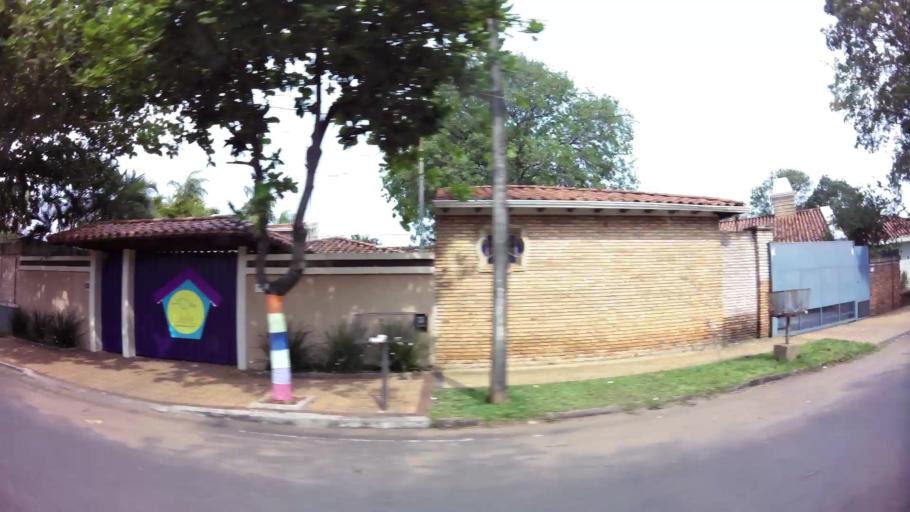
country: PY
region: Central
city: Fernando de la Mora
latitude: -25.2974
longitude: -57.5582
